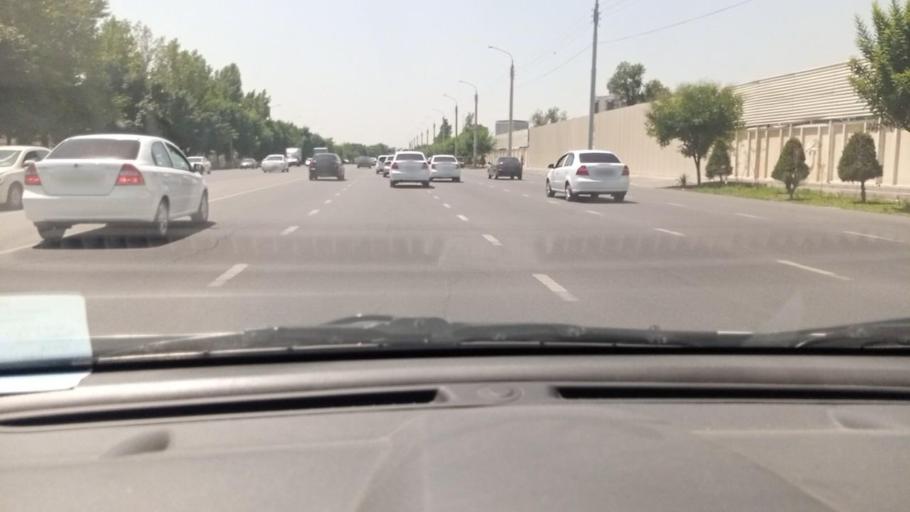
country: UZ
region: Toshkent Shahri
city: Tashkent
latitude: 41.2754
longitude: 69.2703
